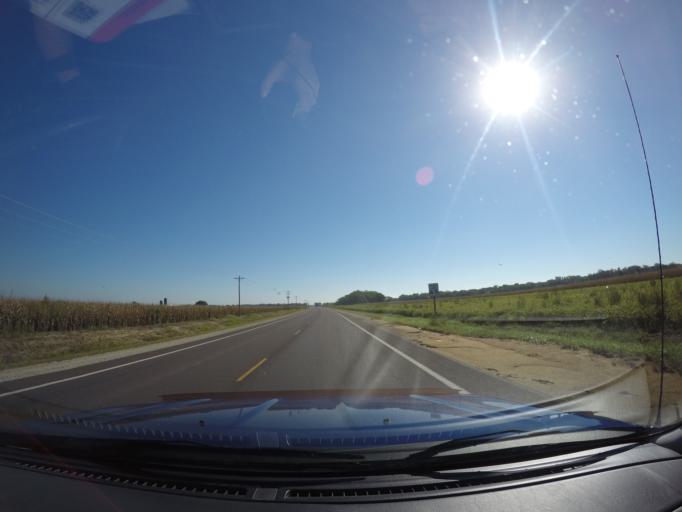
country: US
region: Kansas
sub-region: Pottawatomie County
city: Wamego
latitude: 39.2096
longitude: -96.2565
